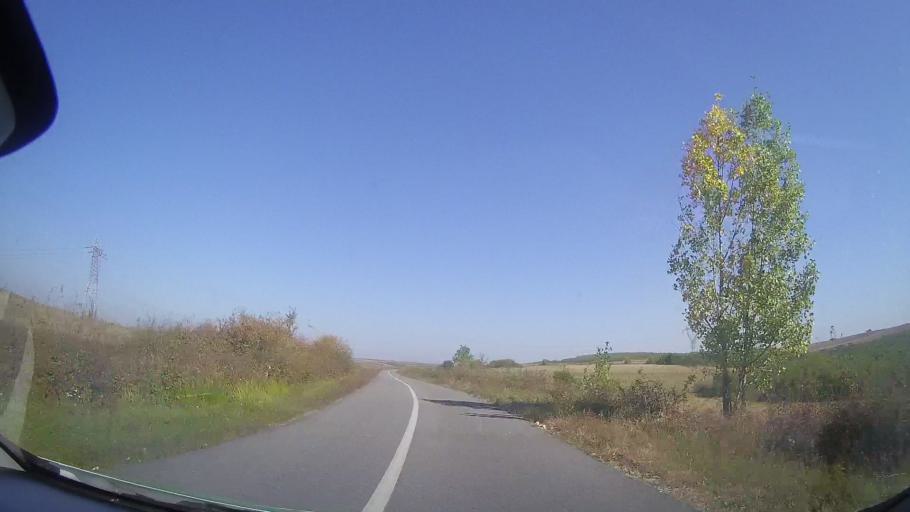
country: RO
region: Timis
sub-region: Comuna Balint
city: Balint
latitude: 45.8268
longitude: 21.8521
